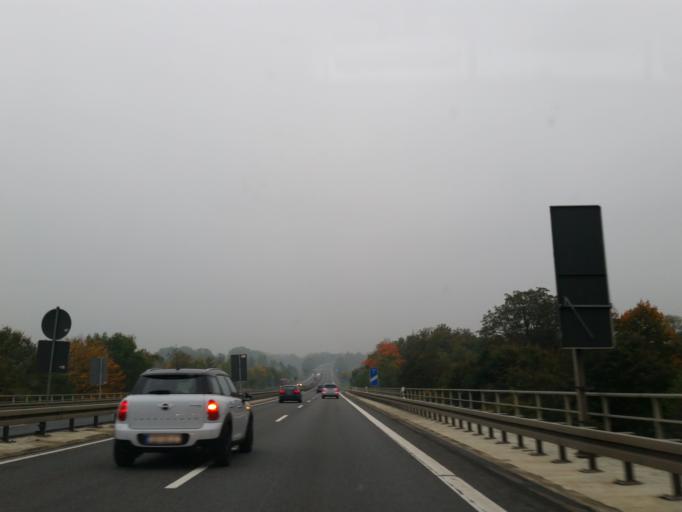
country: DE
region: Lower Saxony
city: Vienenburg
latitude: 51.9604
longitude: 10.5777
